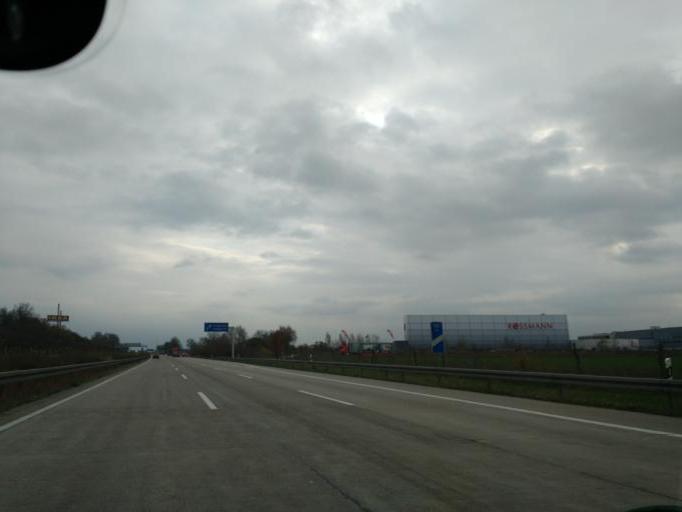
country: DE
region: Lower Saxony
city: Isernhagen Farster Bauerschaft
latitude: 52.4949
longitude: 9.8327
